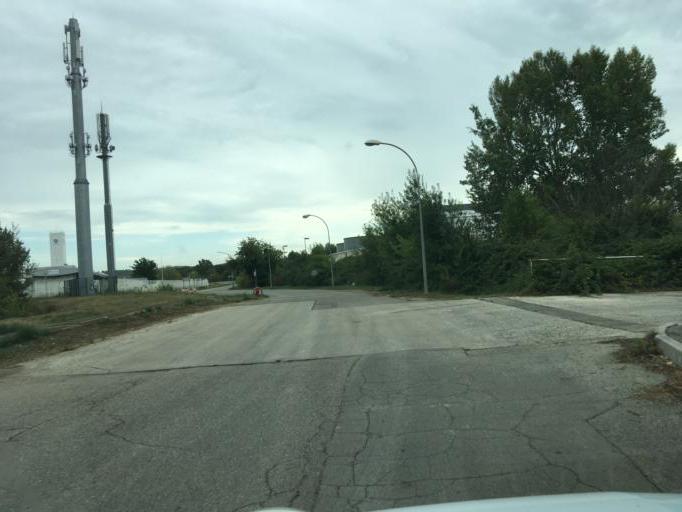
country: FR
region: Provence-Alpes-Cote d'Azur
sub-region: Departement des Bouches-du-Rhone
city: Rousset
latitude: 43.4738
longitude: 5.6013
